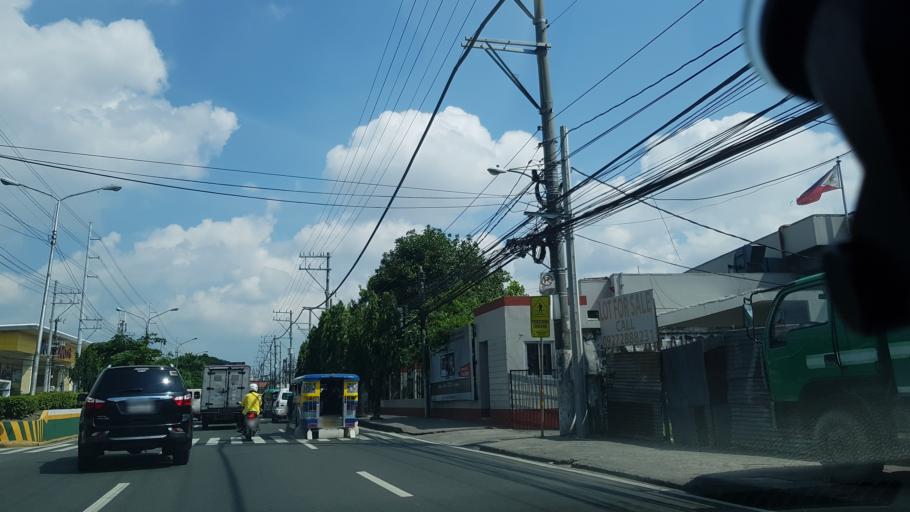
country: PH
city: Sambayanihan People's Village
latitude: 14.4727
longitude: 121.0047
